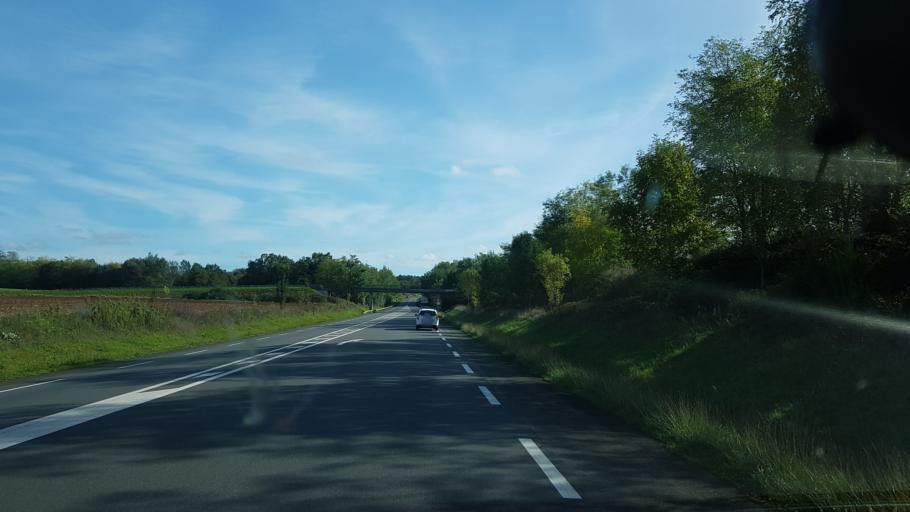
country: FR
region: Poitou-Charentes
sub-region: Departement de la Charente
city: Chasseneuil-sur-Bonnieure
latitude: 45.8367
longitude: 0.4644
